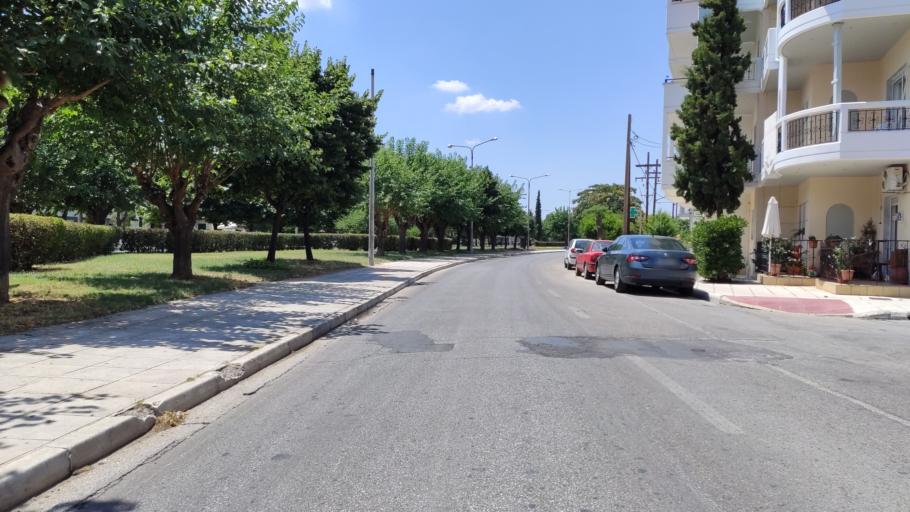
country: GR
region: East Macedonia and Thrace
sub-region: Nomos Rodopis
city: Komotini
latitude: 41.1163
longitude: 25.3945
